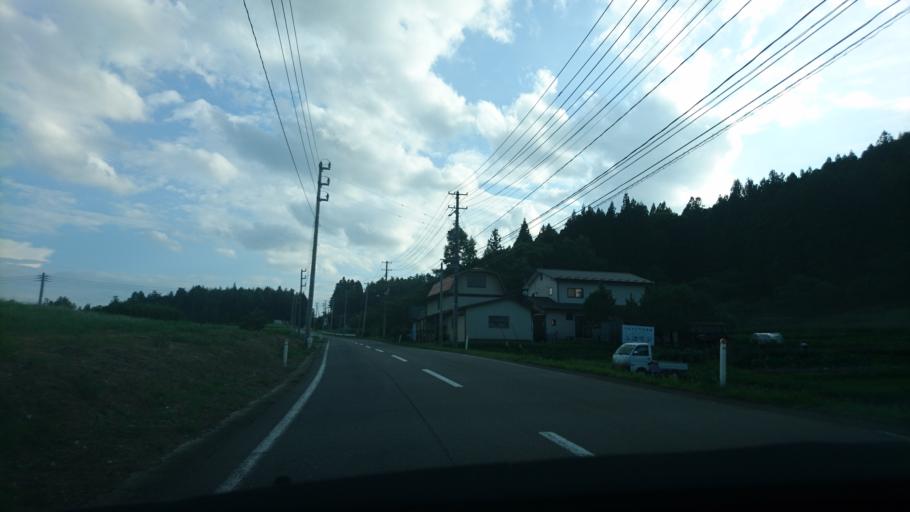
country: JP
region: Iwate
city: Ichinoseki
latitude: 39.0128
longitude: 141.2876
